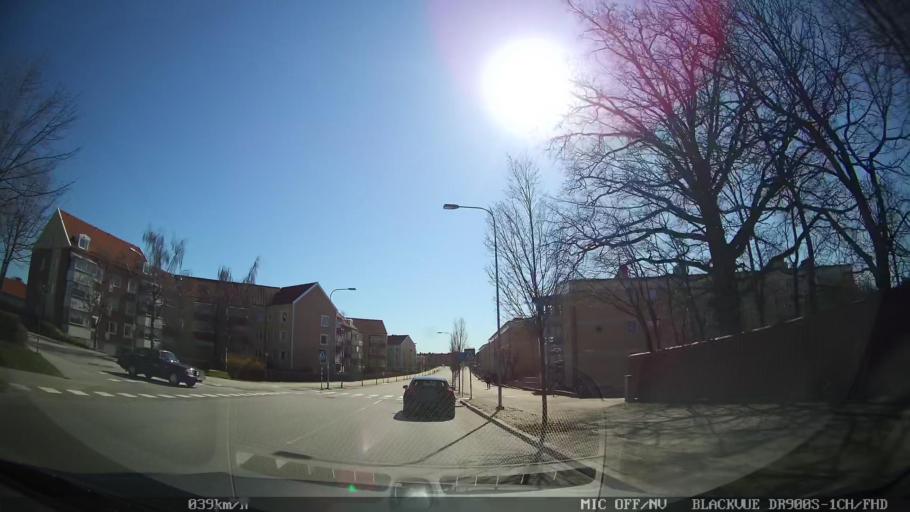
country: SE
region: Skane
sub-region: Ystads Kommun
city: Ystad
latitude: 55.4320
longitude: 13.8028
